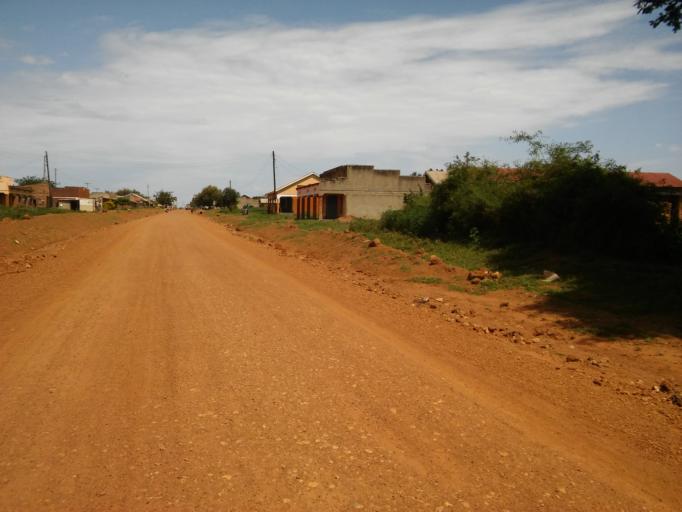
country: UG
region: Eastern Region
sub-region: Kumi District
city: Kumi
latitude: 1.4724
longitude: 33.8699
